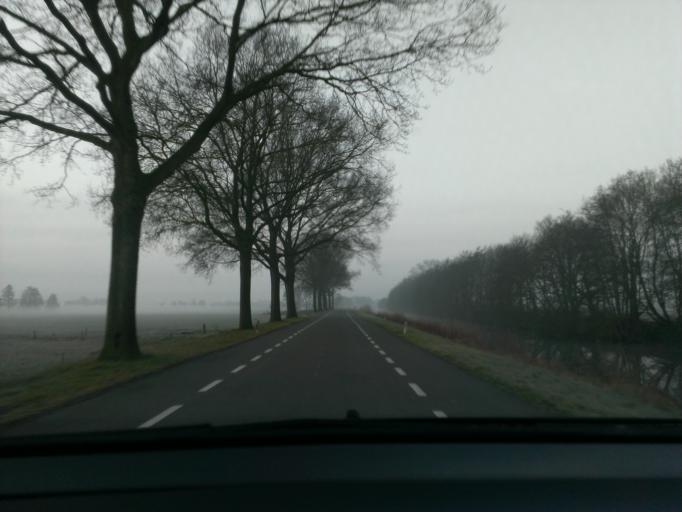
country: NL
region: Gelderland
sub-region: Gemeente Epe
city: Epe
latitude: 52.3239
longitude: 6.0129
